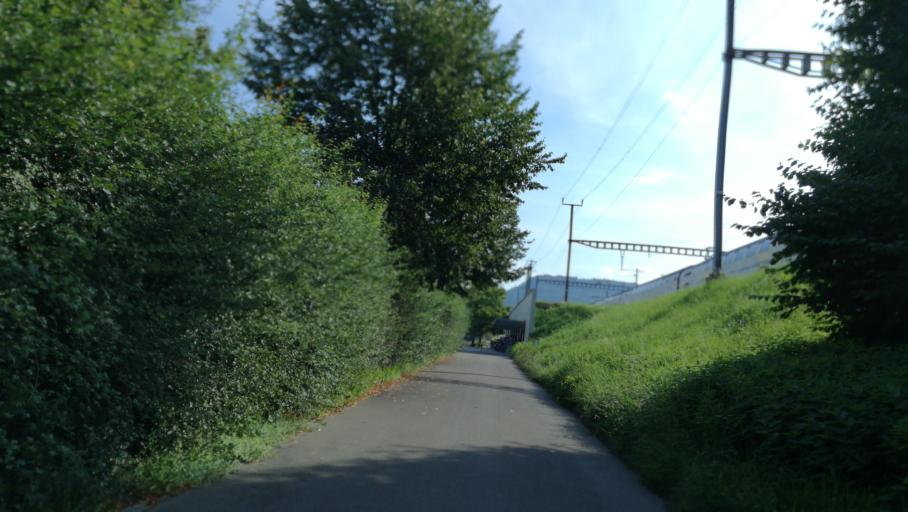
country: CH
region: Zug
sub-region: Zug
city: Baar
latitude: 47.1952
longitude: 8.5217
